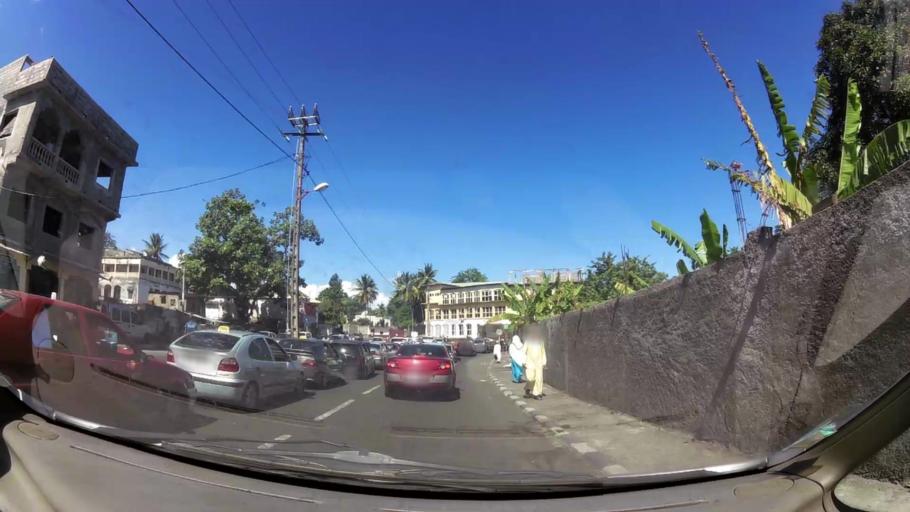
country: KM
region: Grande Comore
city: Moroni
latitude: -11.7020
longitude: 43.2554
